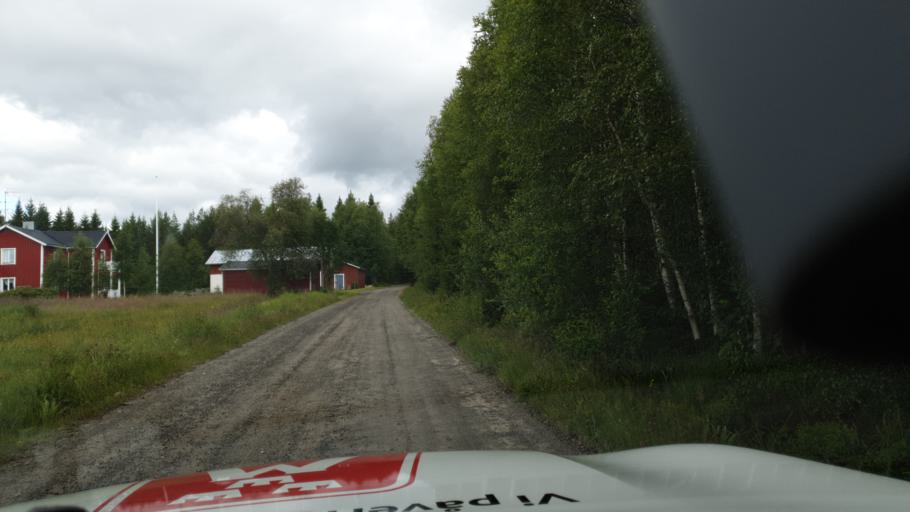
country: SE
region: Vaesterbotten
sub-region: Robertsfors Kommun
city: Robertsfors
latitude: 64.2274
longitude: 21.0569
